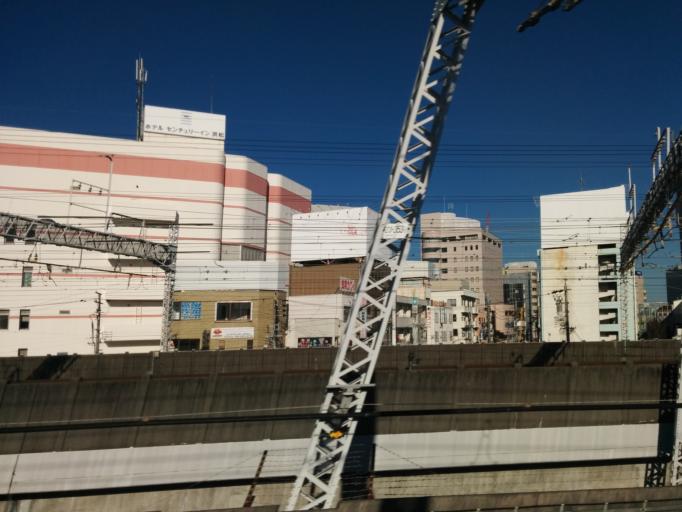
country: JP
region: Shizuoka
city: Hamamatsu
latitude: 34.7021
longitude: 137.7322
